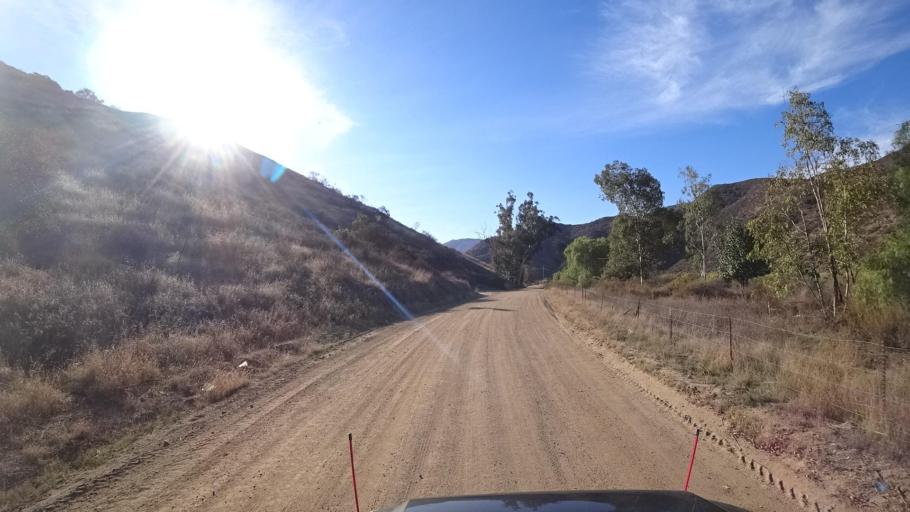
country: US
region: California
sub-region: San Diego County
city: Crest
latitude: 32.7774
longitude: -116.8516
